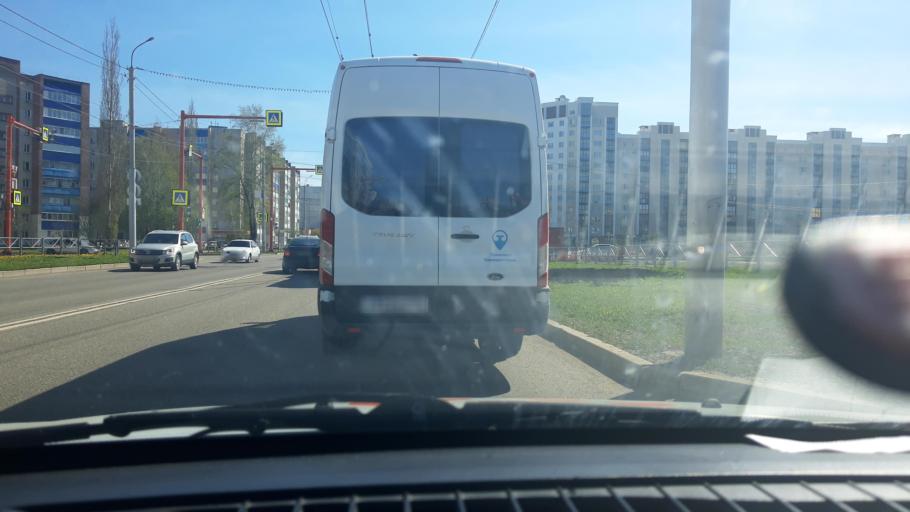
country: RU
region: Bashkortostan
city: Sterlitamak
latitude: 53.6306
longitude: 55.9034
